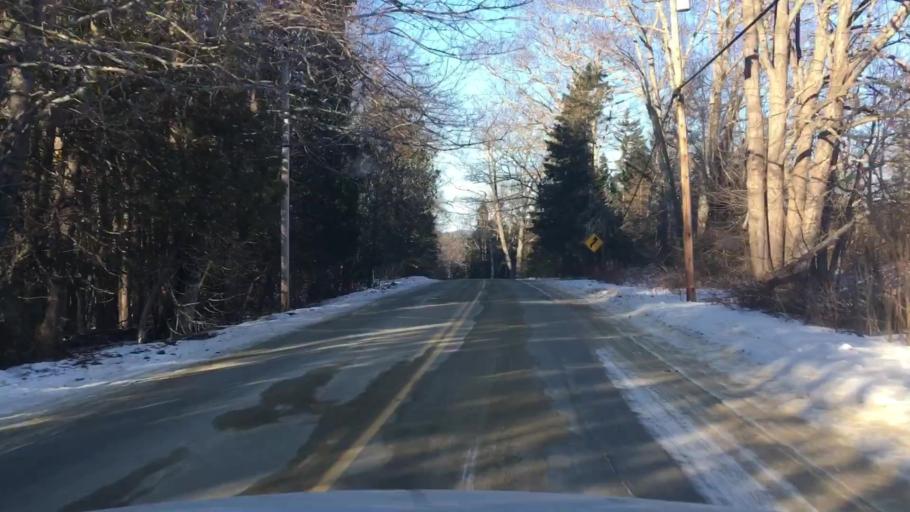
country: US
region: Maine
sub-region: Hancock County
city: Castine
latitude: 44.3774
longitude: -68.7518
